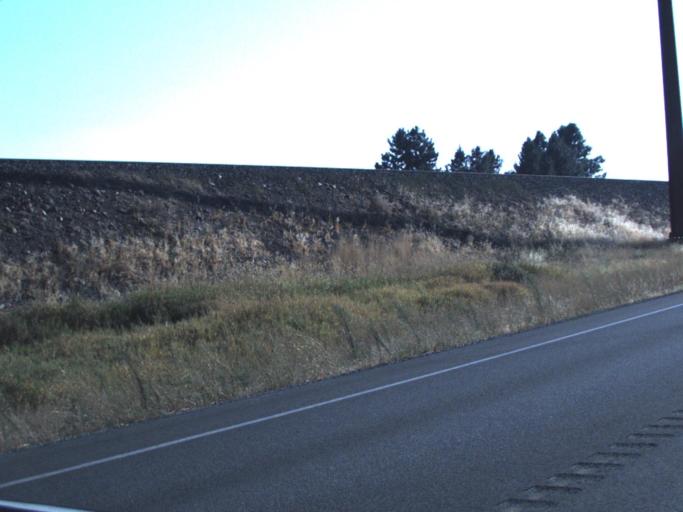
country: US
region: Washington
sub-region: Spokane County
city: Otis Orchards-East Farms
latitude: 47.7175
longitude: -117.0841
